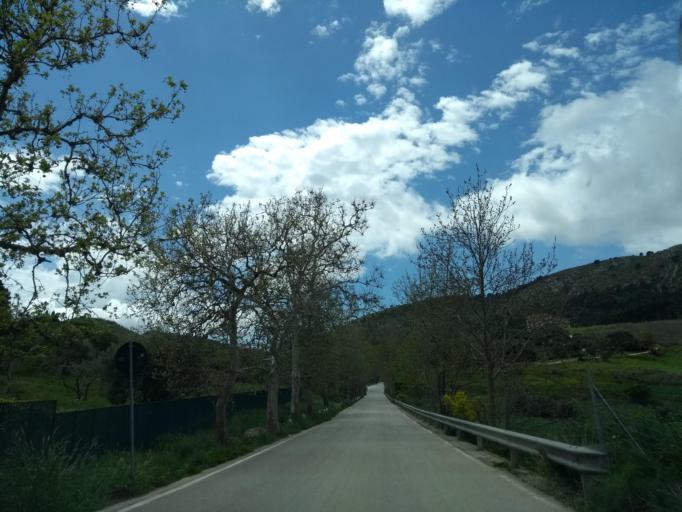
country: IT
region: Sicily
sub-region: Trapani
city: Calatafimi
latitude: 37.9434
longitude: 12.8383
